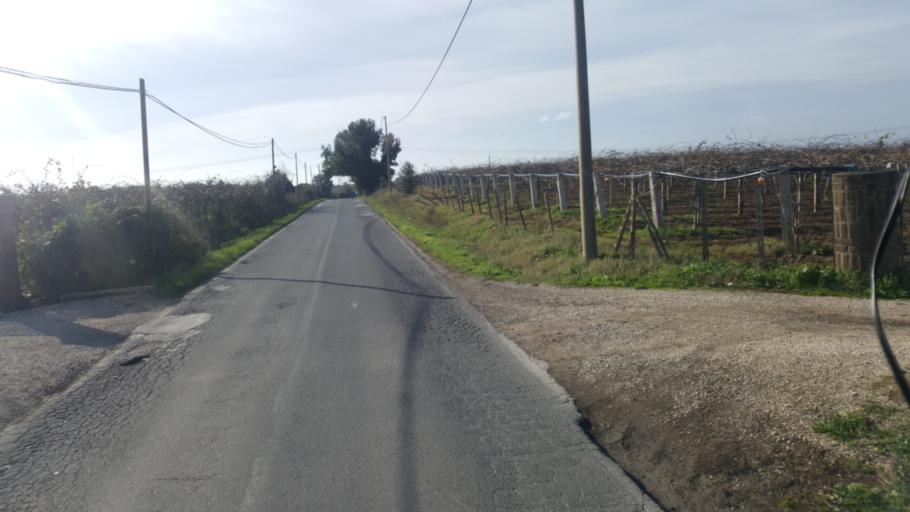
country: IT
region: Latium
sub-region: Provincia di Latina
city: Campoleone
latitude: 41.6437
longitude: 12.6217
